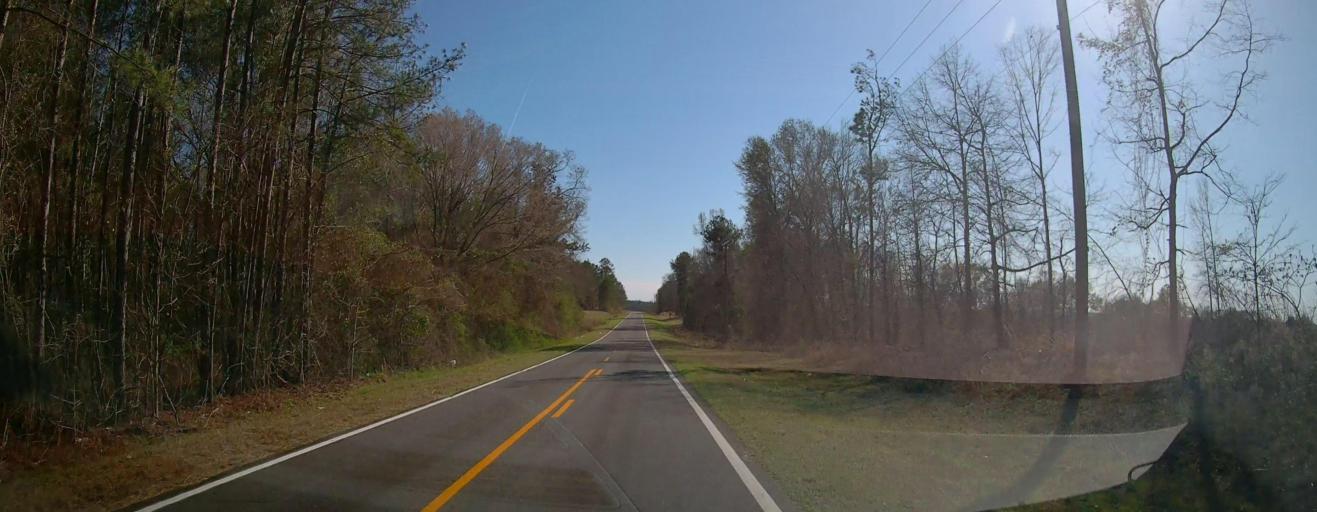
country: US
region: Georgia
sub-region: Taylor County
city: Reynolds
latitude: 32.5725
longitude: -83.9980
